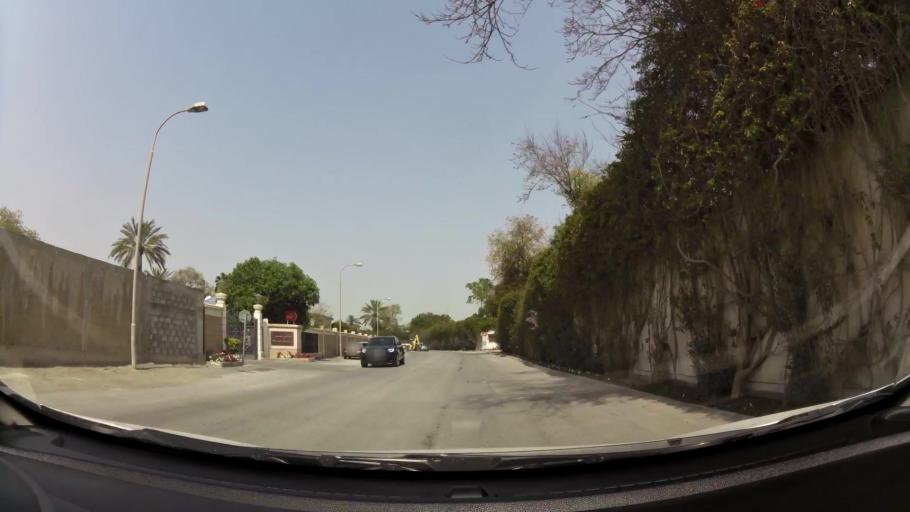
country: BH
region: Manama
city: Jidd Hafs
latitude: 26.2227
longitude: 50.4982
